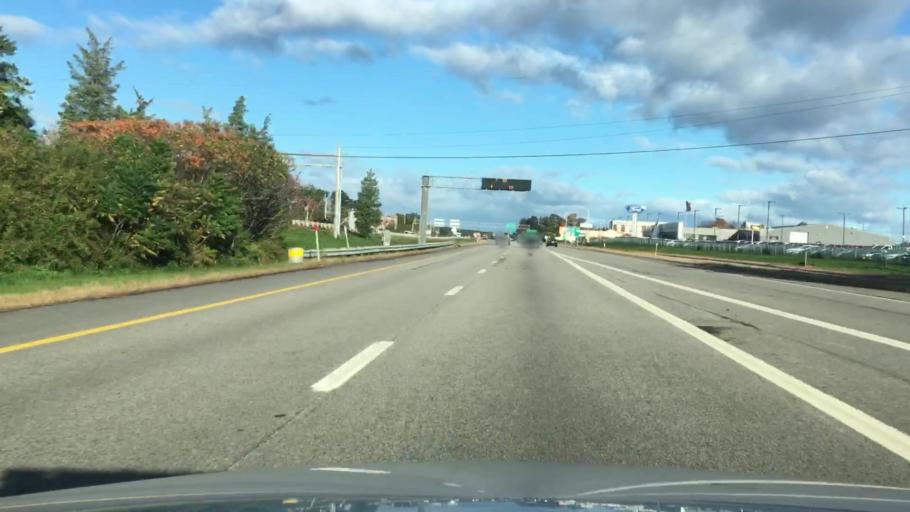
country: US
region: Maine
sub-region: York County
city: South Eliot
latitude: 43.0820
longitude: -70.7927
